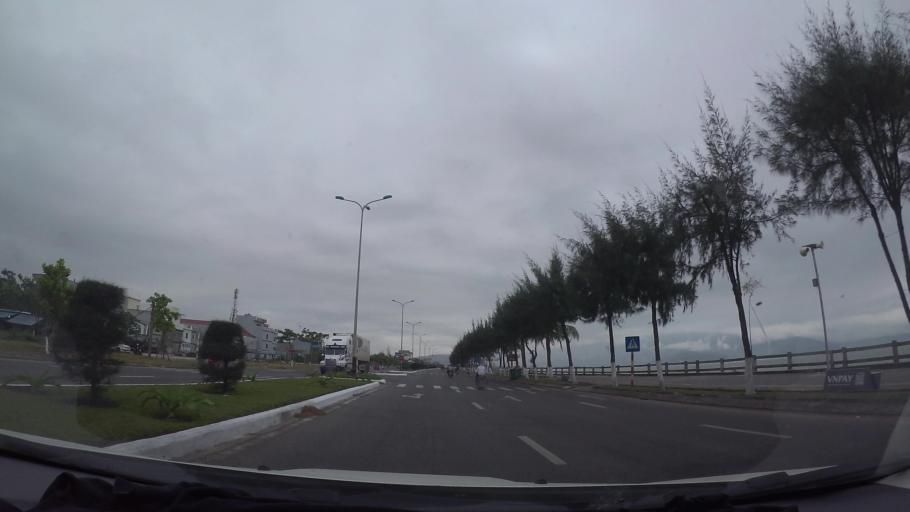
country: VN
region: Da Nang
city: Lien Chieu
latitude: 16.0839
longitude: 108.1618
